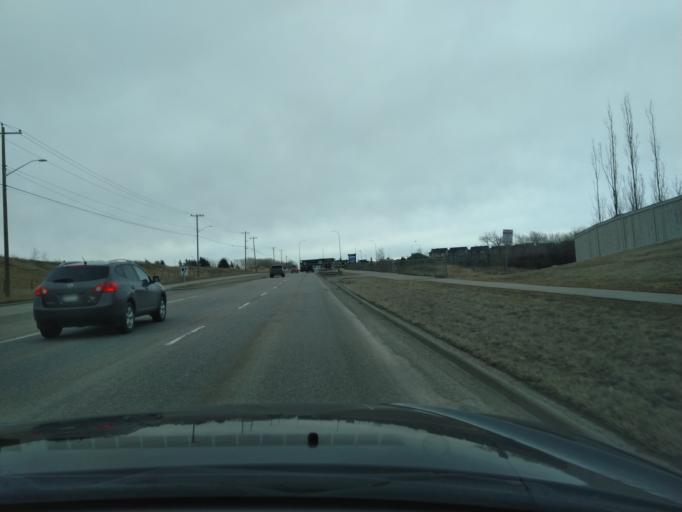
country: CA
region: Alberta
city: Calgary
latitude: 51.1540
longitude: -114.2231
